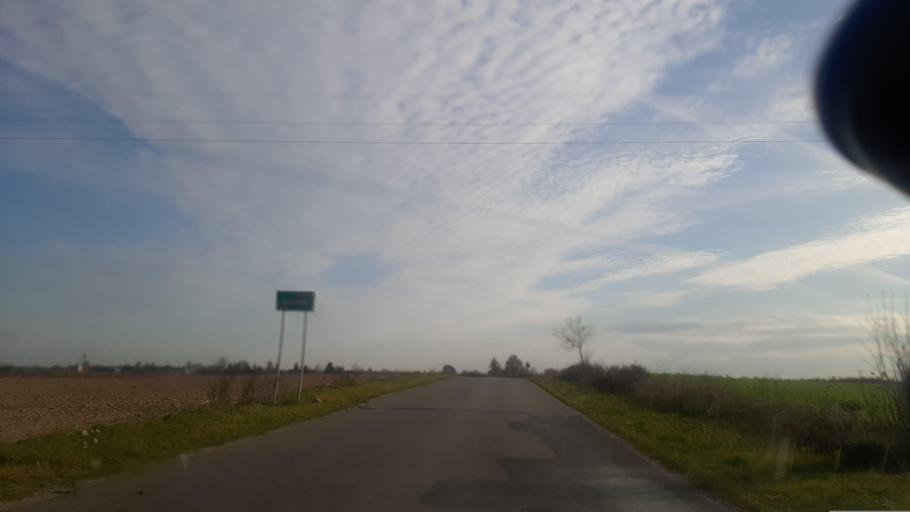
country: PL
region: Lublin Voivodeship
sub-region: Powiat lubelski
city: Garbow
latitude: 51.3875
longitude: 22.3700
